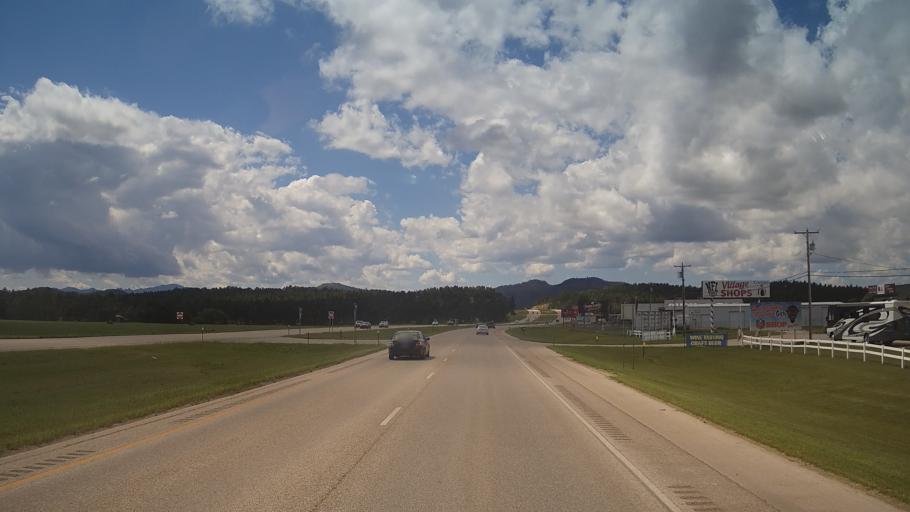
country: US
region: South Dakota
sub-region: Pennington County
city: Colonial Pine Hills
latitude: 43.9705
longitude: -103.3294
